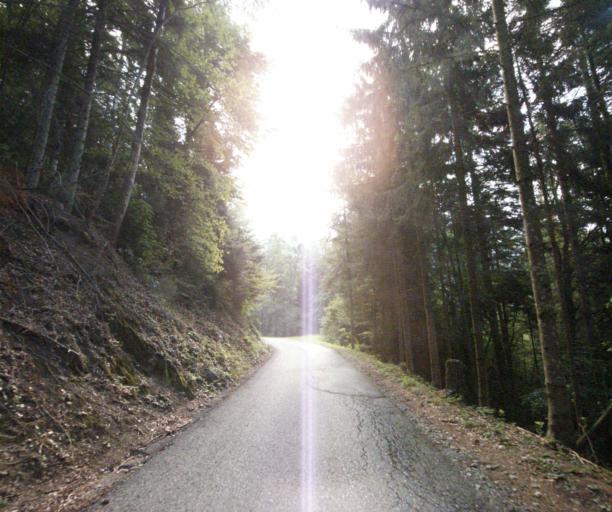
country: CH
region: Vaud
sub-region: Aigle District
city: Villeneuve
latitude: 46.4081
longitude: 6.9403
